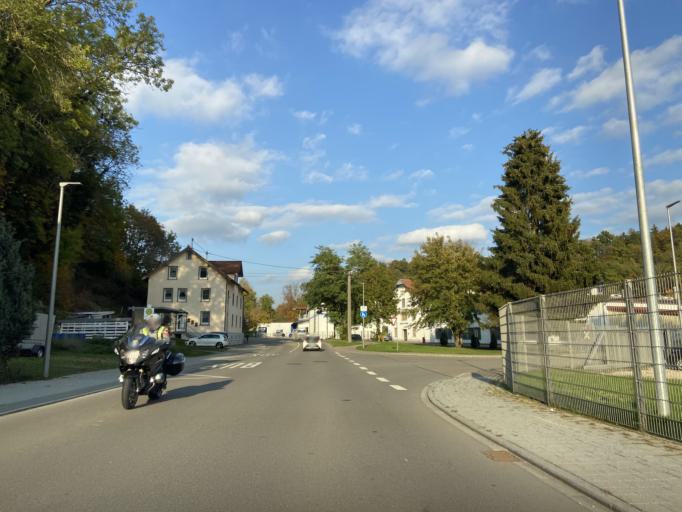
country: DE
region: Baden-Wuerttemberg
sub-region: Tuebingen Region
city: Sigmaringendorf
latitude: 48.0711
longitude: 9.2654
